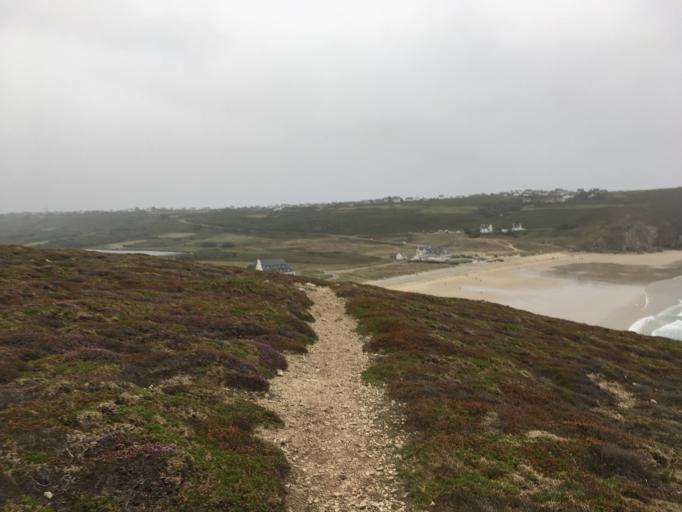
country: FR
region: Brittany
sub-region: Departement du Finistere
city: Plogoff
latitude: 48.0510
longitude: -4.7078
